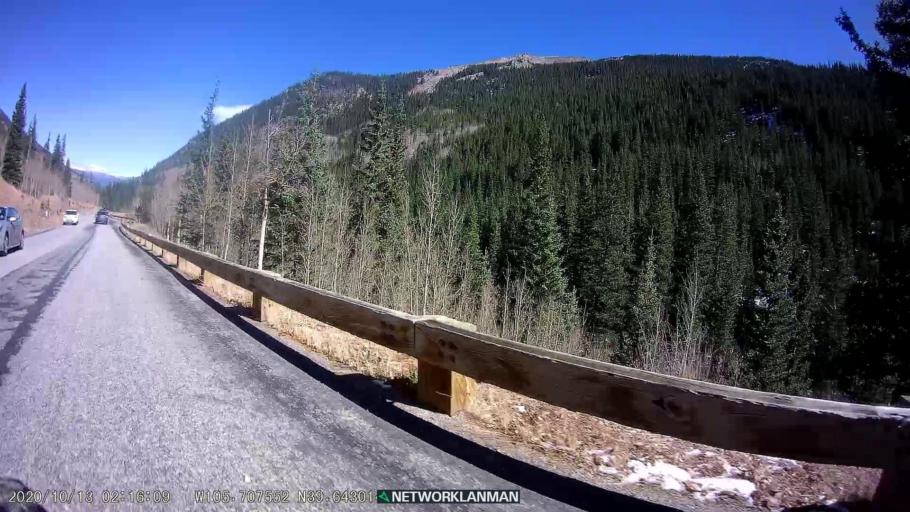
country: US
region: Colorado
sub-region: Clear Creek County
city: Georgetown
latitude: 39.6432
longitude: -105.7077
